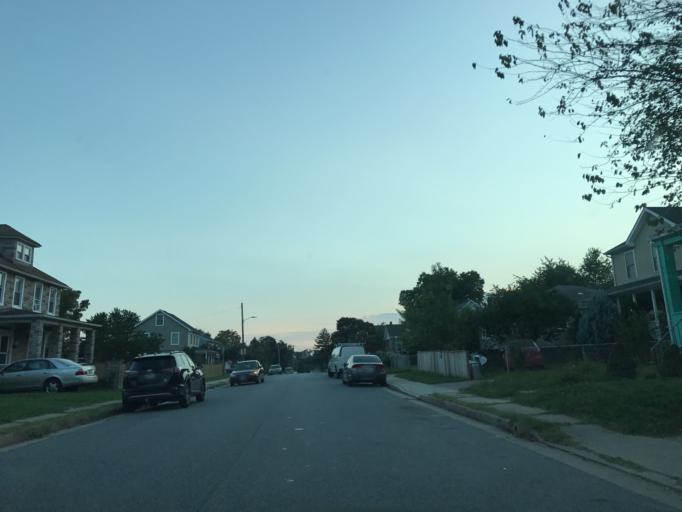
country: US
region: Maryland
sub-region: Baltimore County
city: Dundalk
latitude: 39.2763
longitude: -76.5281
